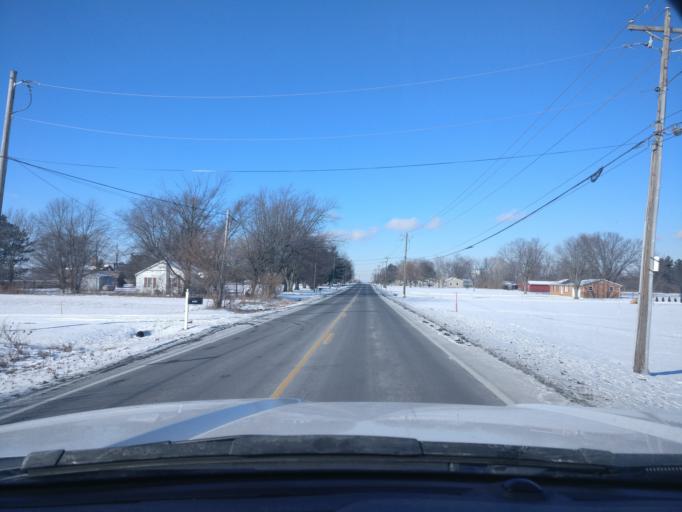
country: US
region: Ohio
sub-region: Warren County
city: Hunter
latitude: 39.5018
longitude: -84.2604
